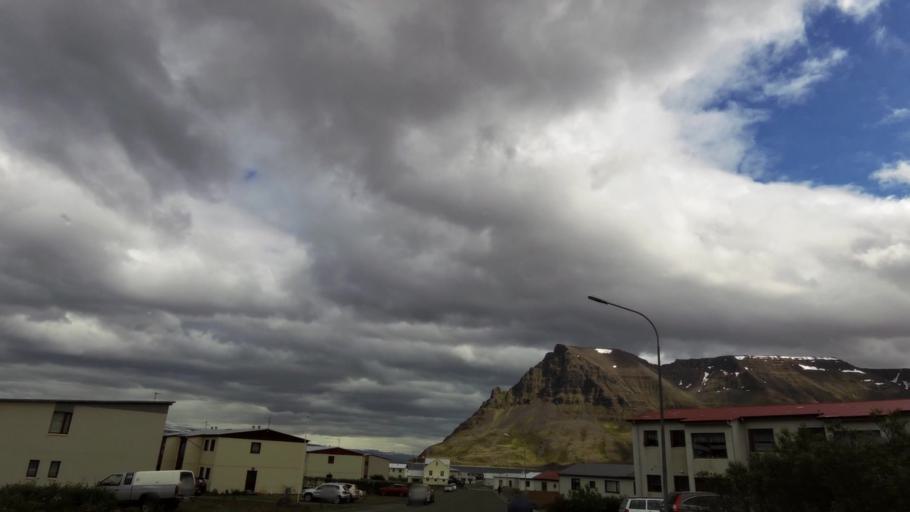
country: IS
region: Westfjords
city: Isafjoerdur
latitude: 66.1575
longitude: -23.2556
